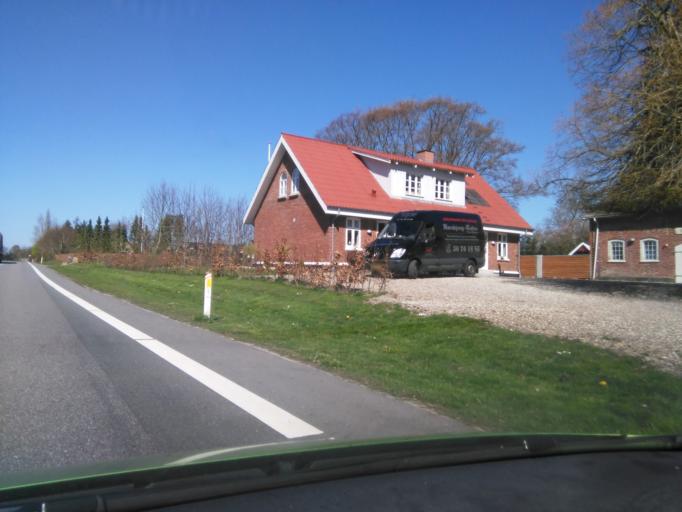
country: DK
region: South Denmark
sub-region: Billund Kommune
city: Grindsted
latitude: 55.6978
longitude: 8.8374
